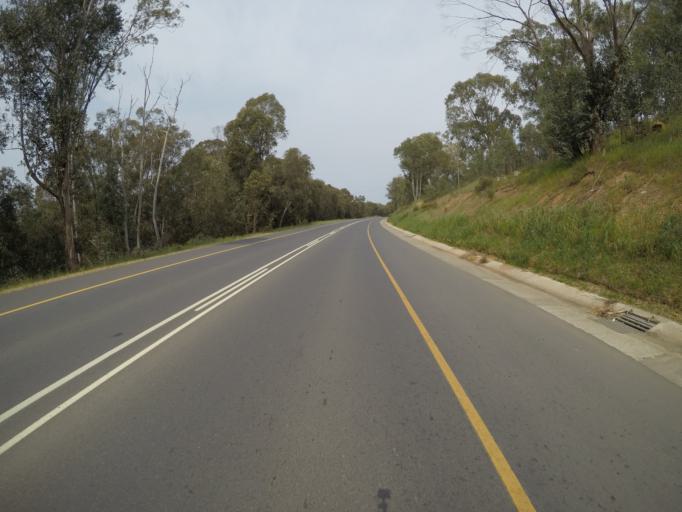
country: ZA
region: Western Cape
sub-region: West Coast District Municipality
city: Malmesbury
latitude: -33.4584
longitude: 18.7468
